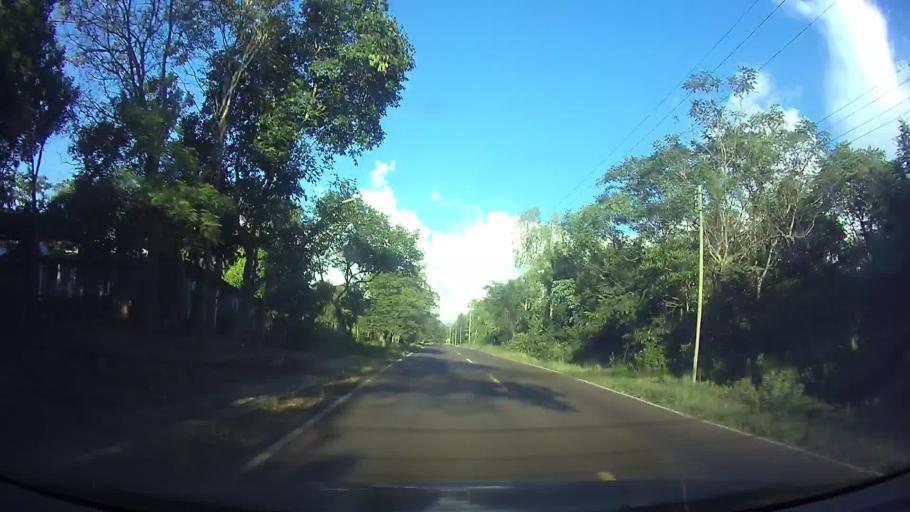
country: PY
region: Cordillera
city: Emboscada
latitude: -25.2018
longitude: -57.3282
